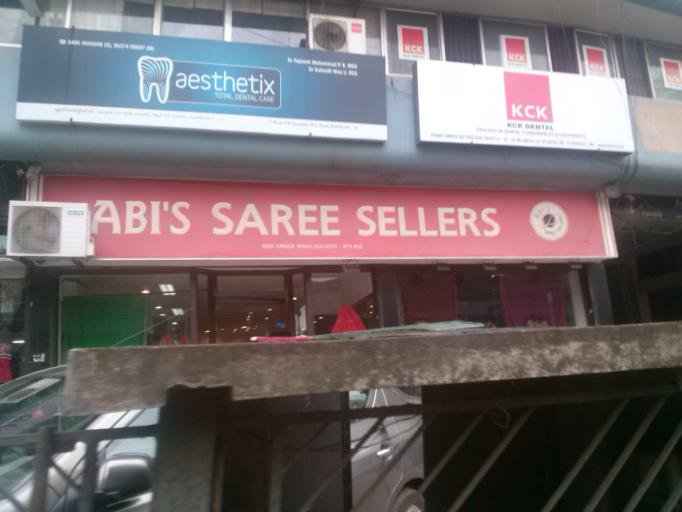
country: IN
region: Kerala
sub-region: Kozhikode
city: Kozhikode
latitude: 11.2564
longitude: 75.7757
